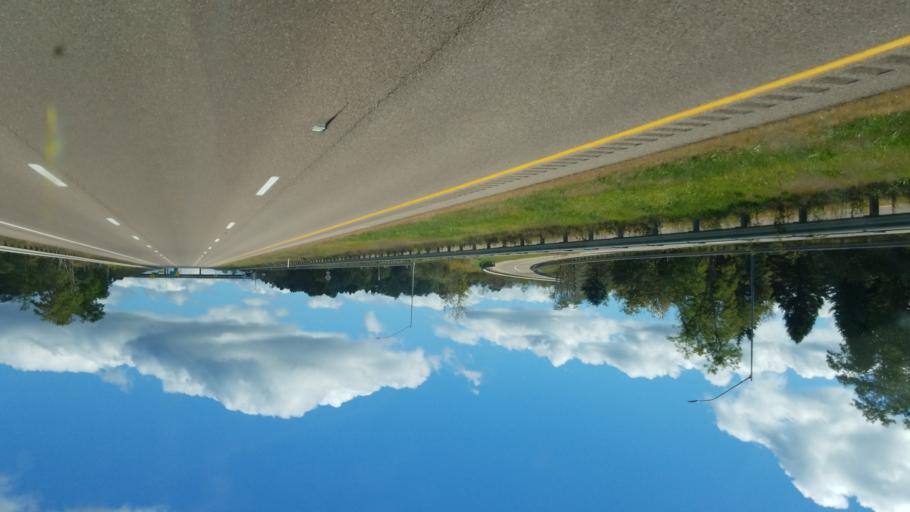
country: US
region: Pennsylvania
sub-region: Somerset County
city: Meyersdale
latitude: 39.6859
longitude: -79.2440
